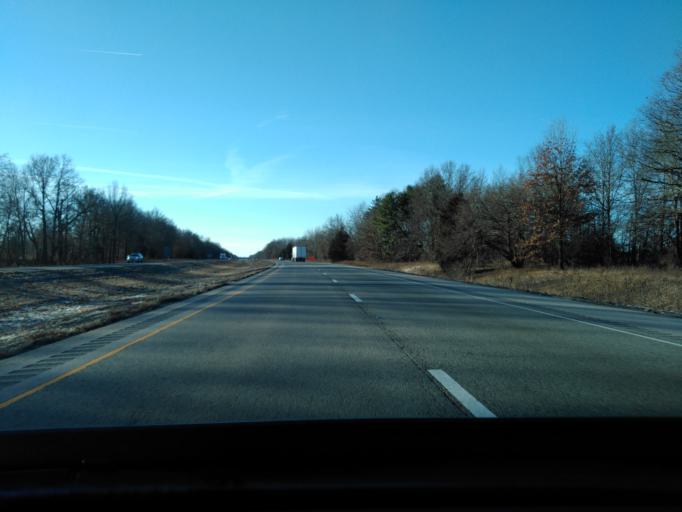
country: US
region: Illinois
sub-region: Franklin County
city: Benton
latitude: 38.0654
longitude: -88.9241
